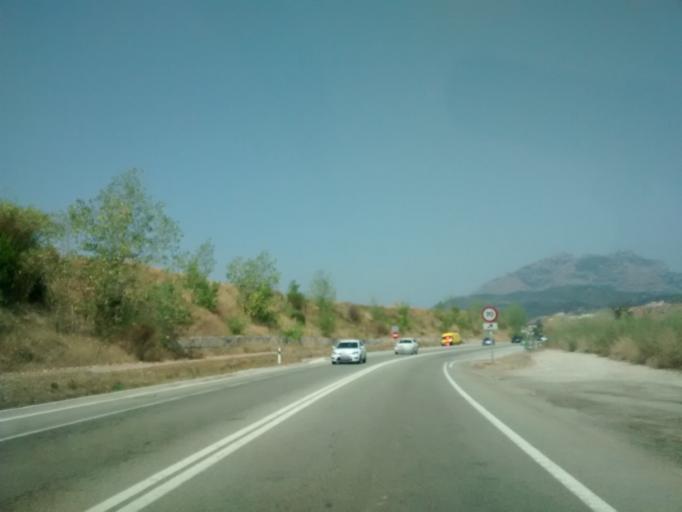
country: ES
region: Catalonia
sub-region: Provincia de Barcelona
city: Olesa de Montserrat
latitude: 41.5323
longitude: 1.9020
